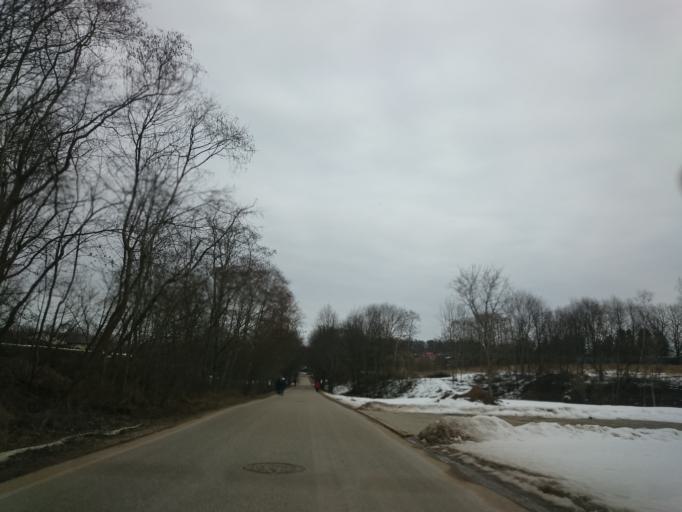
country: LV
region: Cesu Rajons
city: Cesis
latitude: 57.3033
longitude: 25.2544
